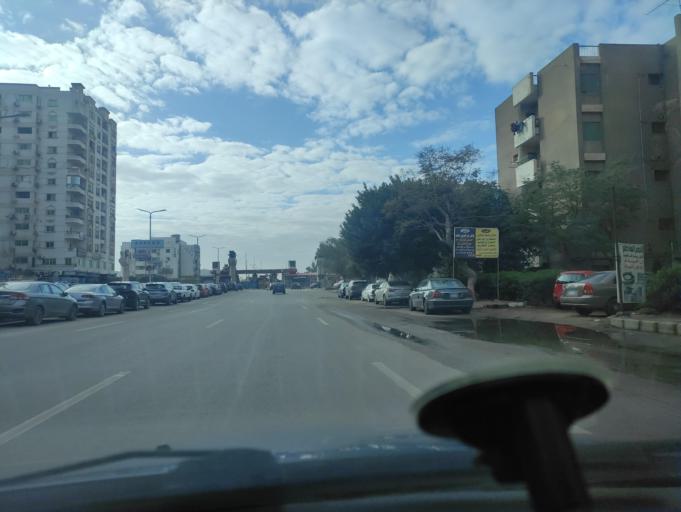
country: EG
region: Muhafazat al Qahirah
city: Cairo
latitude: 30.0474
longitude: 31.3512
